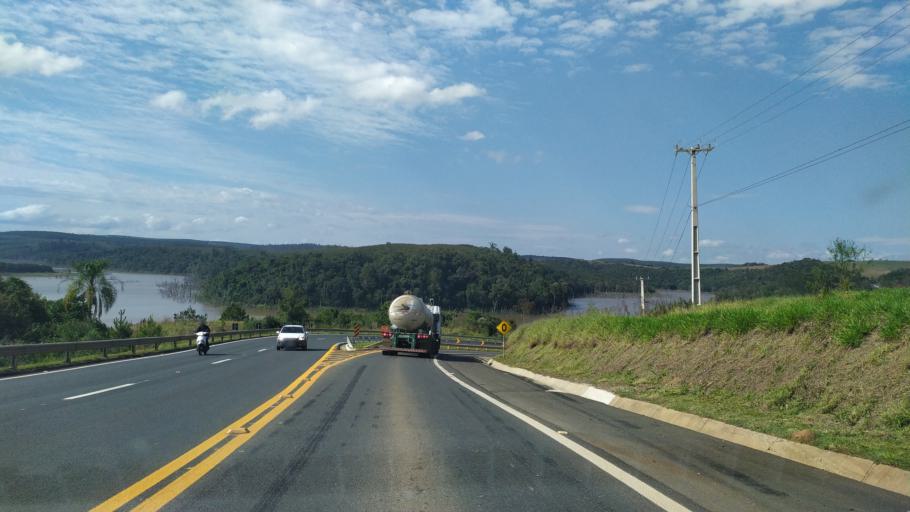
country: BR
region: Parana
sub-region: Telemaco Borba
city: Telemaco Borba
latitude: -24.2610
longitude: -50.7245
